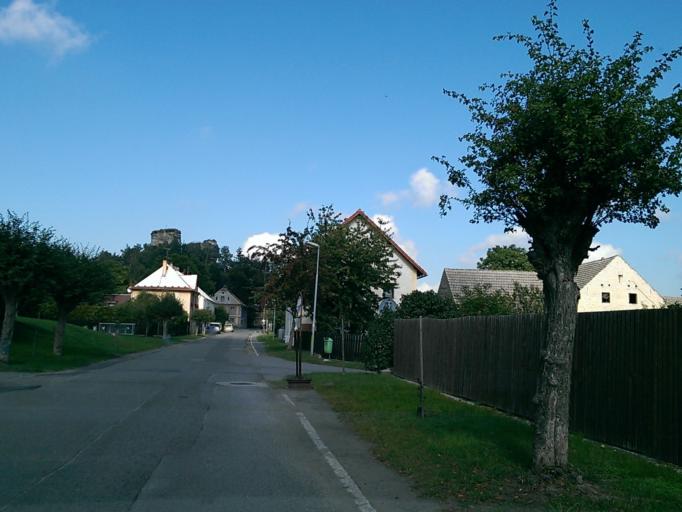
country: CZ
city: Duba
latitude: 50.6087
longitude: 14.5829
